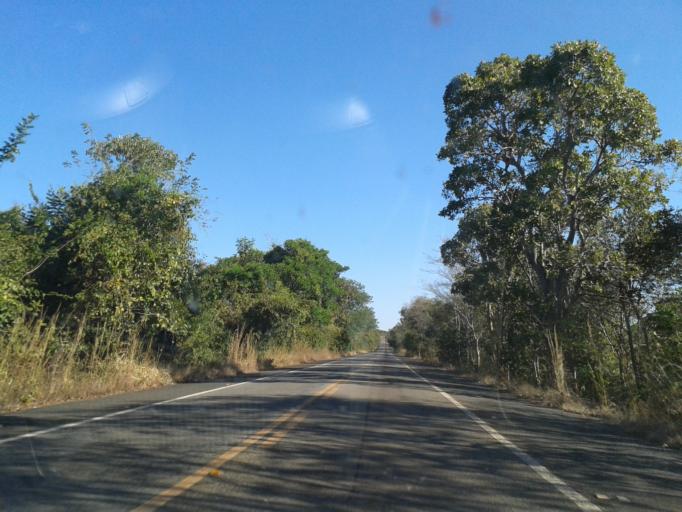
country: BR
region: Goias
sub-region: Mozarlandia
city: Mozarlandia
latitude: -15.0330
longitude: -50.6020
